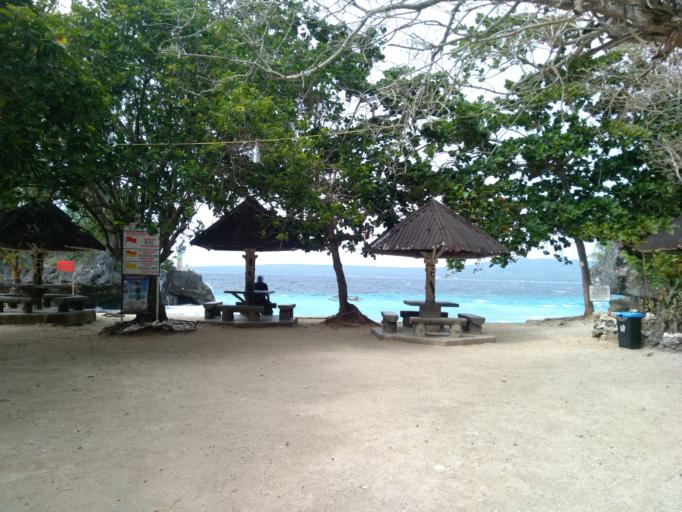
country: PH
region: Central Visayas
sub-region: Province of Siquijor
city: Maria
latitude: 9.2128
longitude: 123.6810
